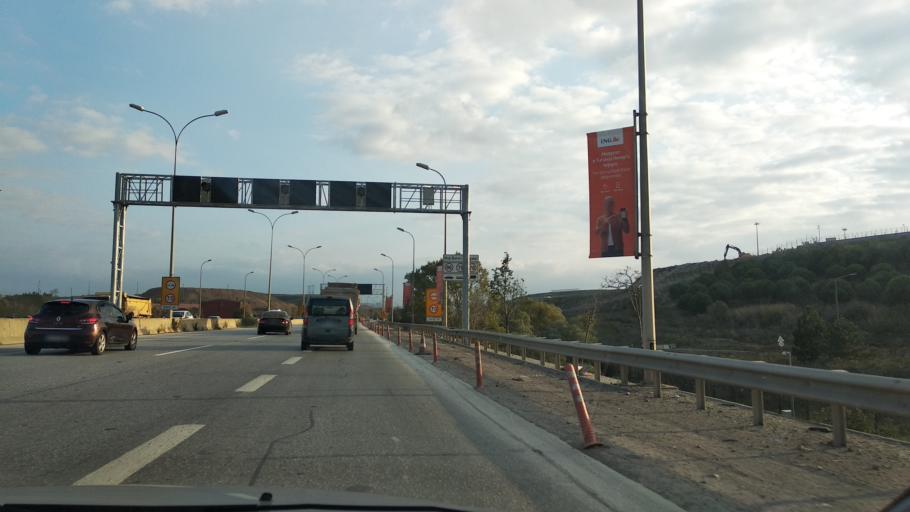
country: TR
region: Istanbul
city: Pendik
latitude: 40.9104
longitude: 29.3265
